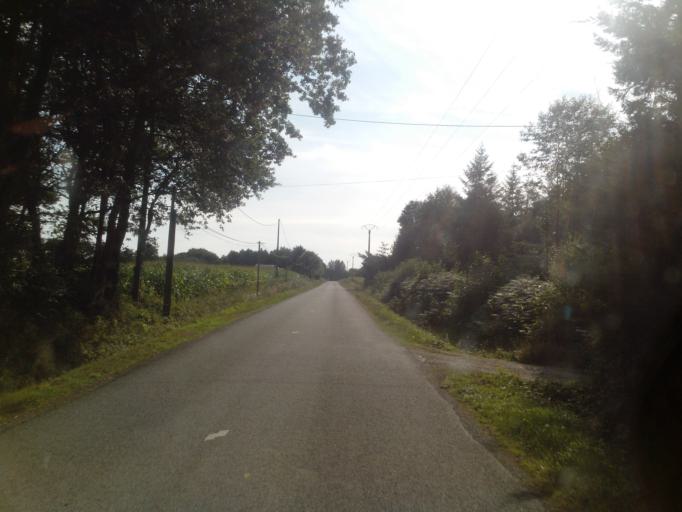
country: FR
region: Brittany
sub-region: Departement du Morbihan
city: Guilliers
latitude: 48.0967
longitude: -2.3565
